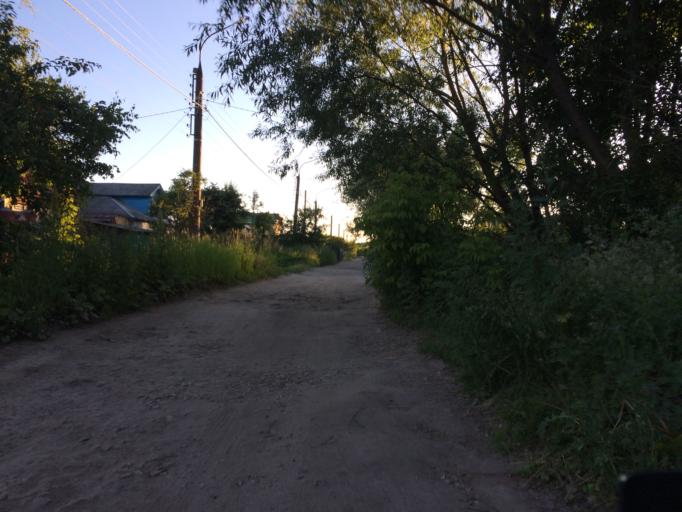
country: RU
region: Mariy-El
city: Yoshkar-Ola
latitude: 56.6532
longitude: 47.8968
